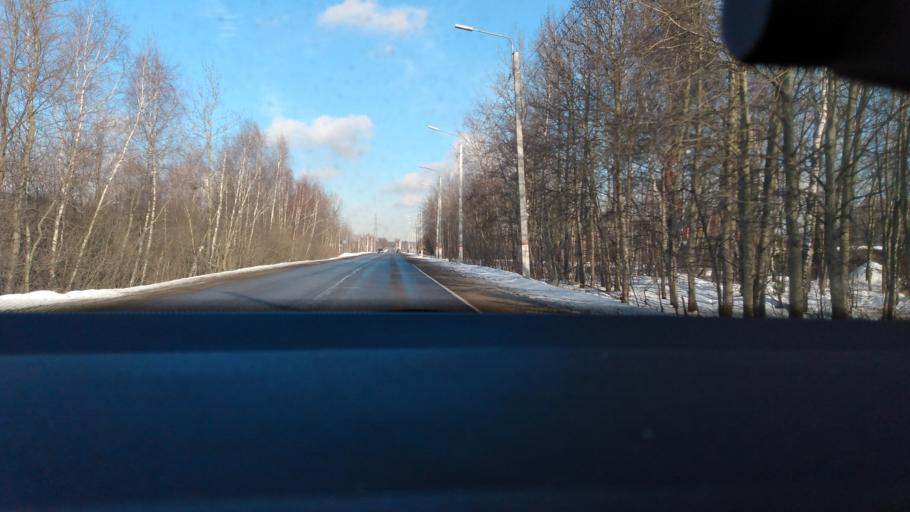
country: RU
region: Moskovskaya
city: Kratovo
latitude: 55.6283
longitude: 38.1597
